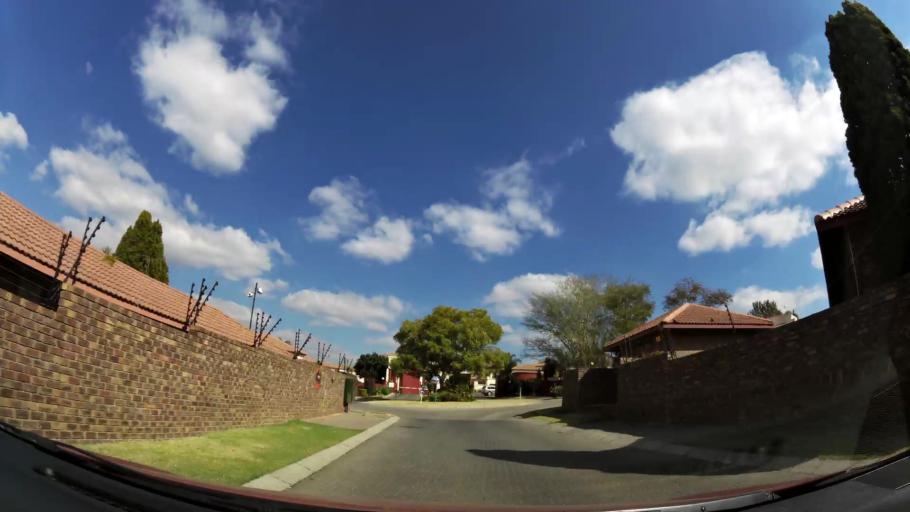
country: ZA
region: Gauteng
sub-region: City of Johannesburg Metropolitan Municipality
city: Roodepoort
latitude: -26.0811
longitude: 27.9488
